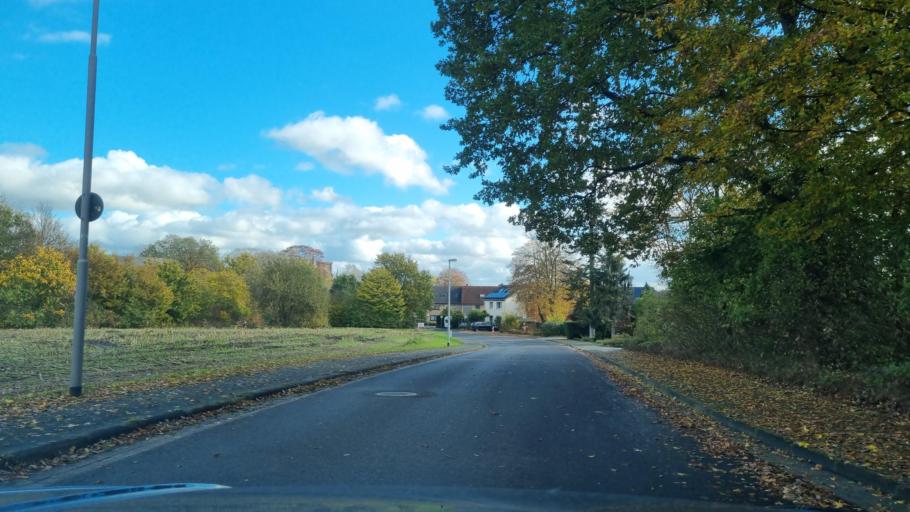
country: DE
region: North Rhine-Westphalia
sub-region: Regierungsbezirk Dusseldorf
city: Kleve
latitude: 51.7750
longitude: 6.1069
